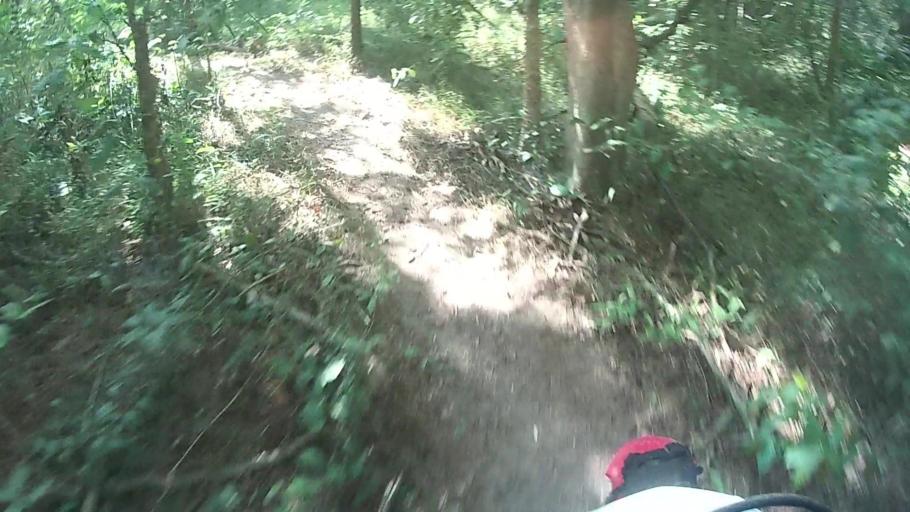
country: TH
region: Chiang Mai
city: San Sai
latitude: 18.9496
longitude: 99.0642
